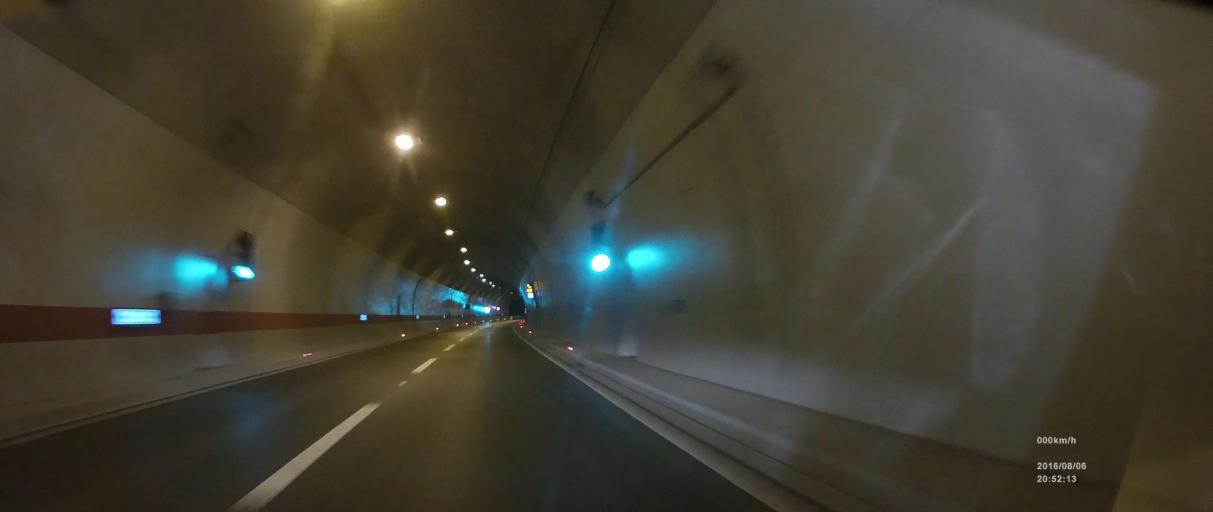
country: BA
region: Federation of Bosnia and Herzegovina
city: Ljubuski
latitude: 43.1260
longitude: 17.4849
